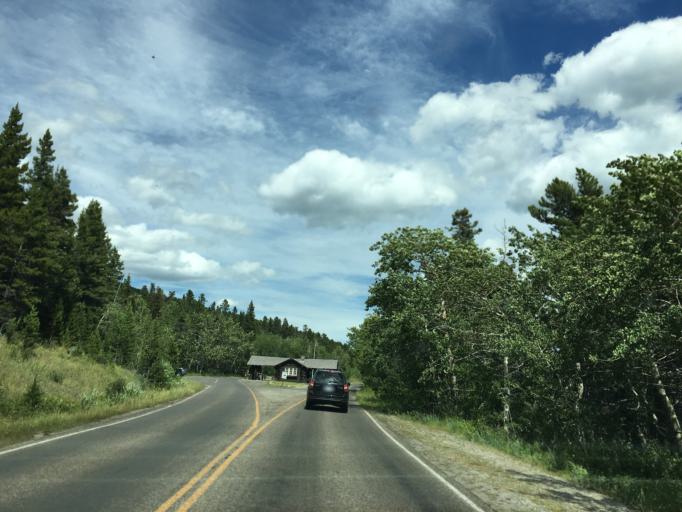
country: CA
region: Alberta
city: Cardston
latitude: 48.8217
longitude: -113.5808
